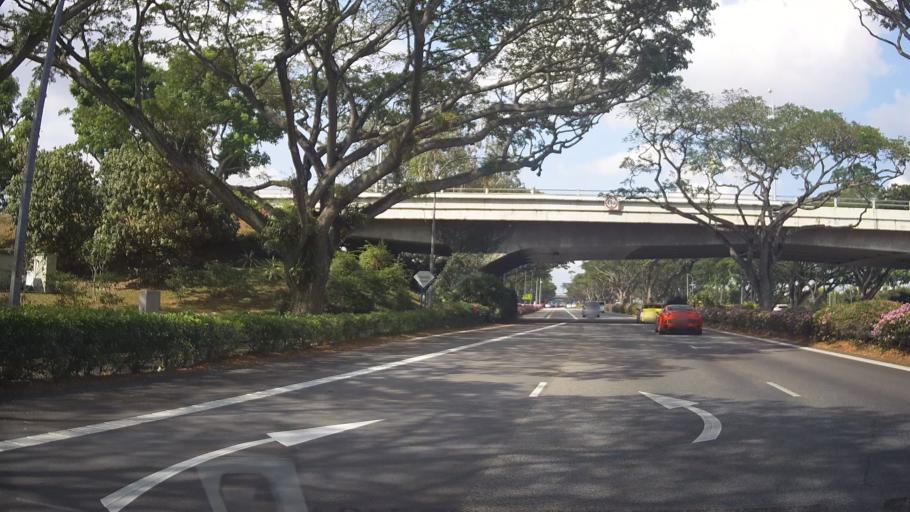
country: SG
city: Singapore
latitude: 1.3364
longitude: 103.9797
